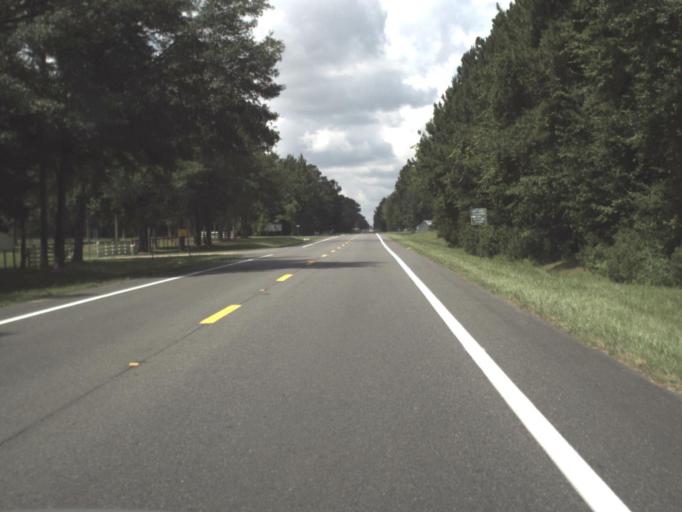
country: US
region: Florida
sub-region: Union County
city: Lake Butler
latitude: 30.0093
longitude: -82.3625
